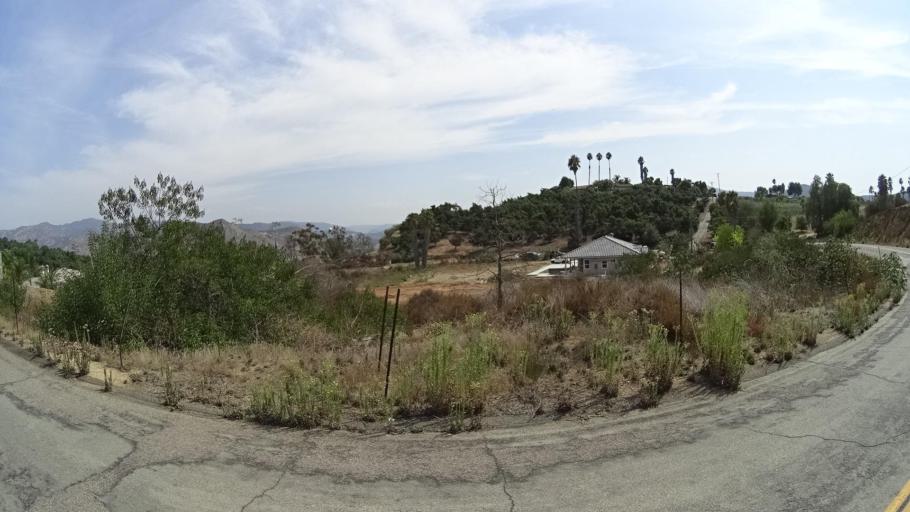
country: US
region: California
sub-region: San Diego County
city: Escondido
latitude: 33.0978
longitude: -117.0316
